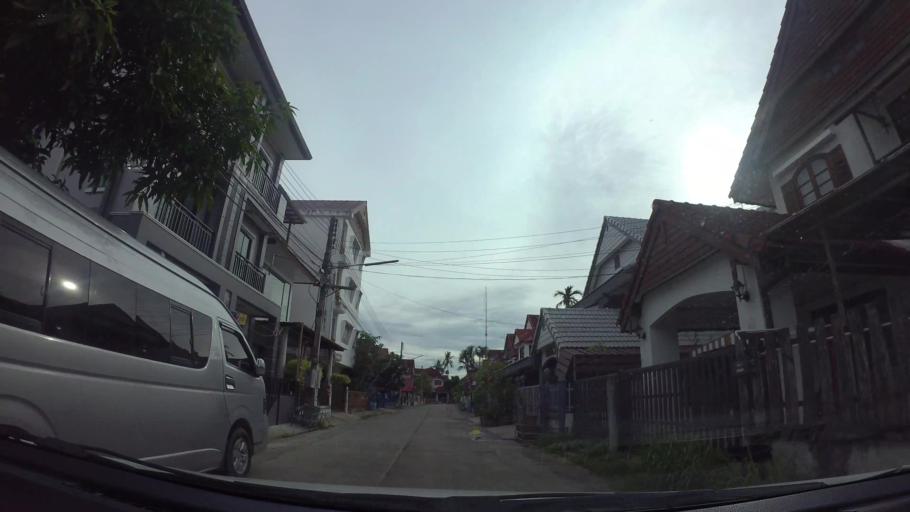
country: TH
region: Chiang Mai
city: Chiang Mai
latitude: 18.7659
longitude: 98.9861
